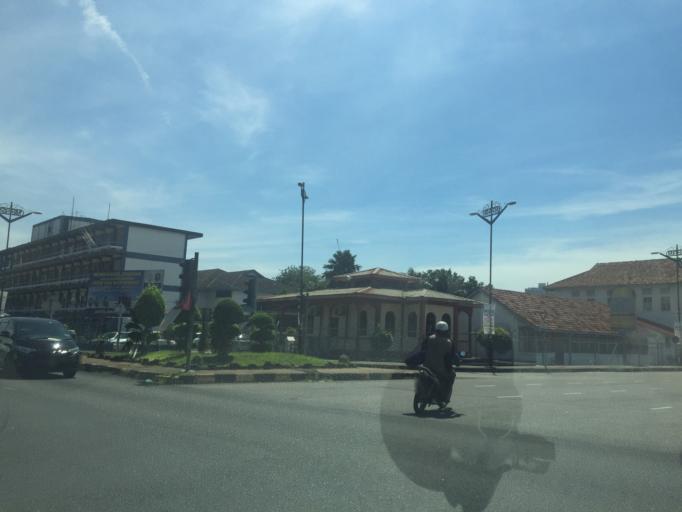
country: MY
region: Penang
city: Butterworth
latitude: 5.4072
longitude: 100.3698
